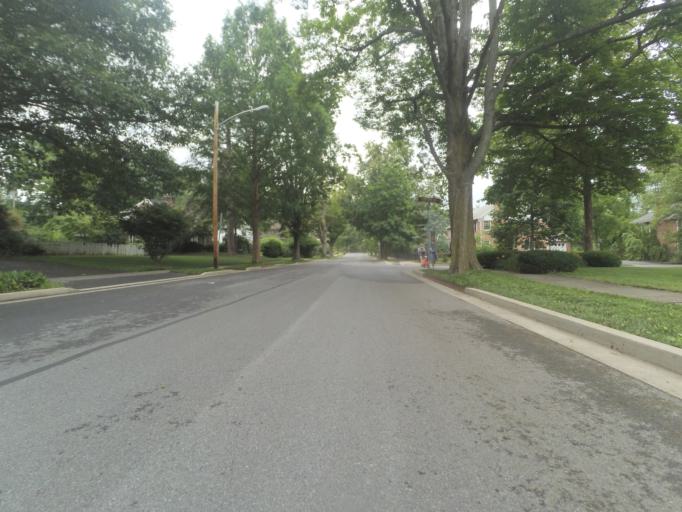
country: US
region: Pennsylvania
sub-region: Centre County
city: State College
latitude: 40.7850
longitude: -77.8658
